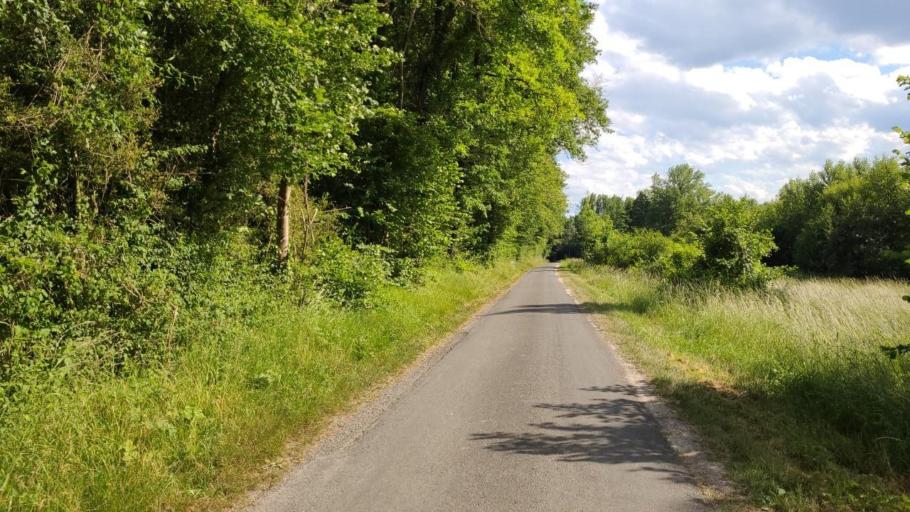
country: FR
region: Centre
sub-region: Departement d'Indre-et-Loire
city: Reugny
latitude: 47.4746
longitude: 0.8884
